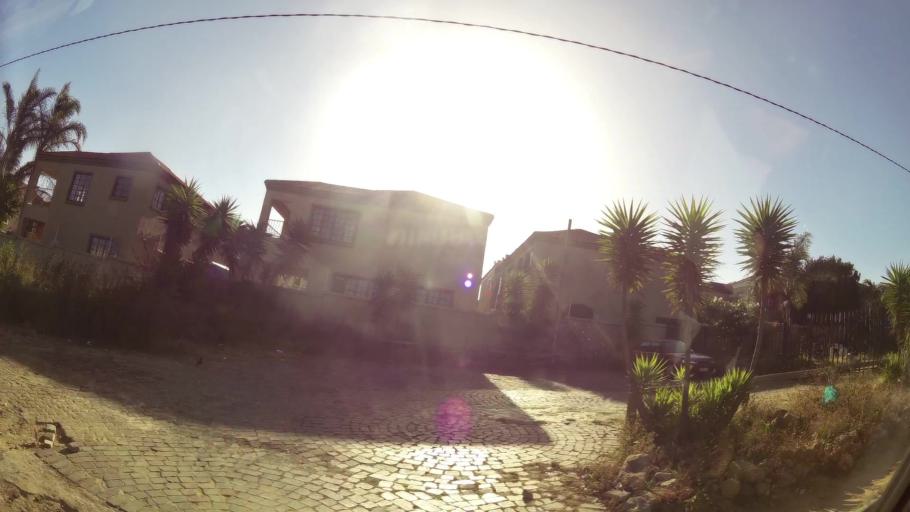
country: ZA
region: Gauteng
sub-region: City of Johannesburg Metropolitan Municipality
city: Diepsloot
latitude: -26.0147
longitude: 27.9974
